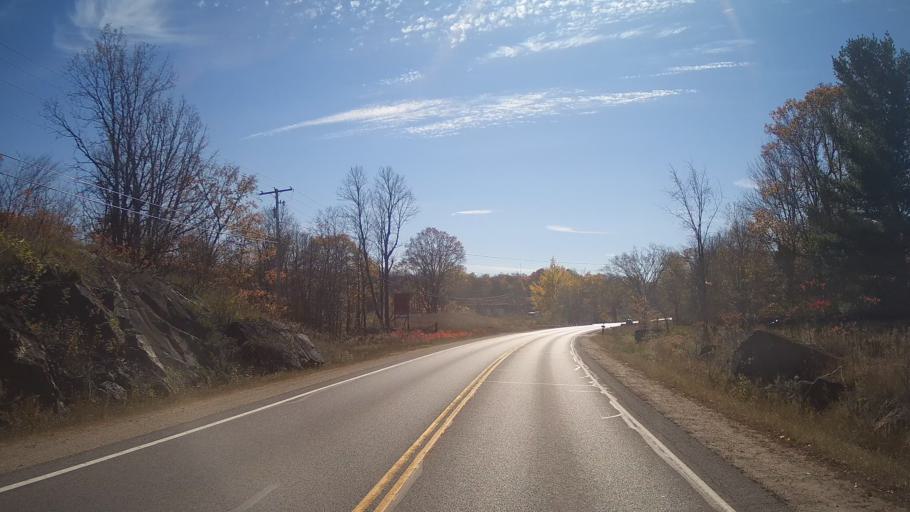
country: CA
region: Ontario
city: Perth
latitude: 44.7565
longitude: -76.6854
